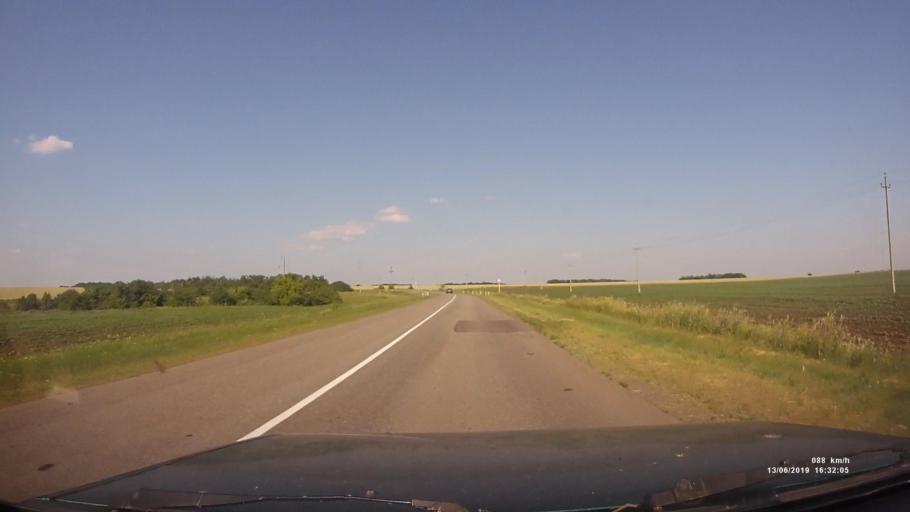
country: RU
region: Rostov
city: Kazanskaya
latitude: 49.8455
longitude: 41.2658
